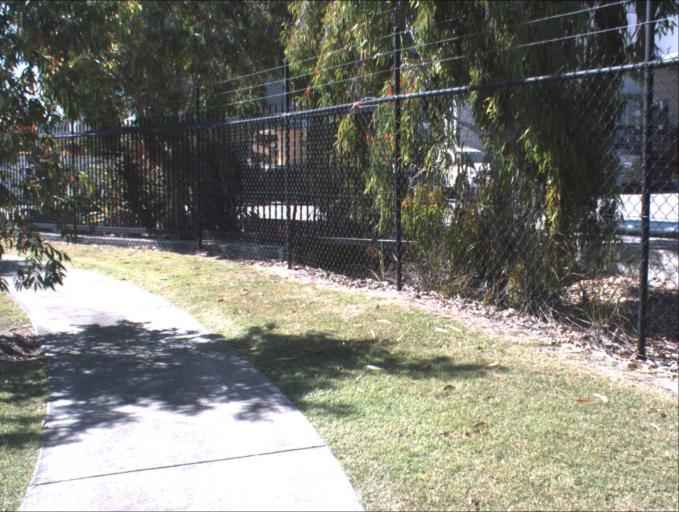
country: AU
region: Queensland
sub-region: Logan
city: Woodridge
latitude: -27.6524
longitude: 153.0745
